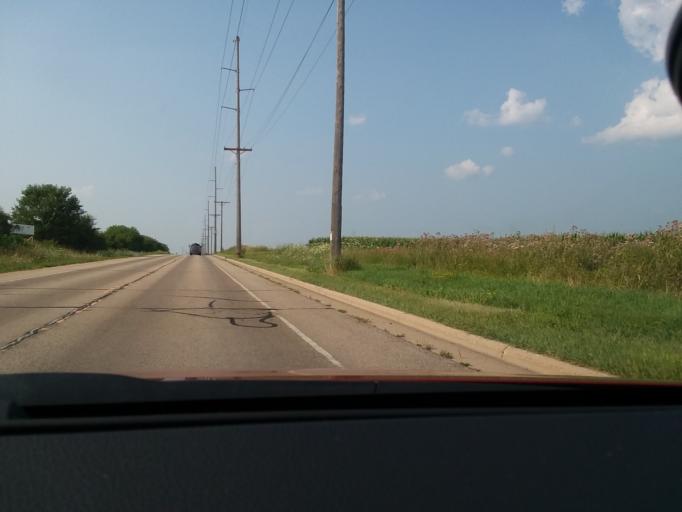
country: US
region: Wisconsin
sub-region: Dane County
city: Cottage Grove
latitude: 43.1138
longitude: -89.2665
